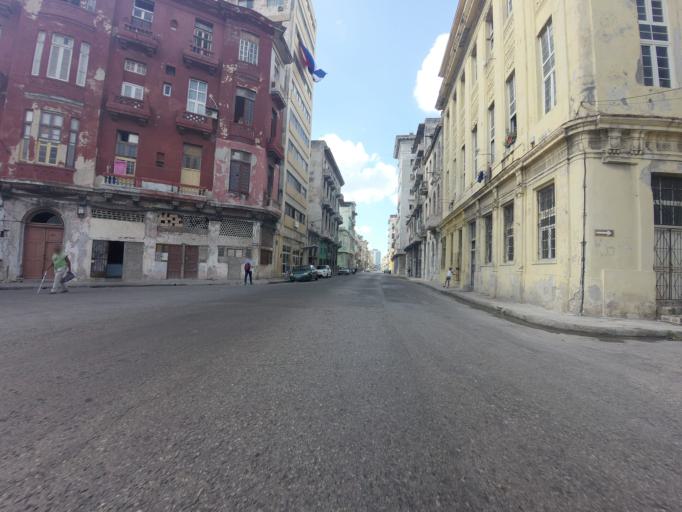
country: CU
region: La Habana
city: Centro Habana
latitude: 23.1415
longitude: -82.3647
